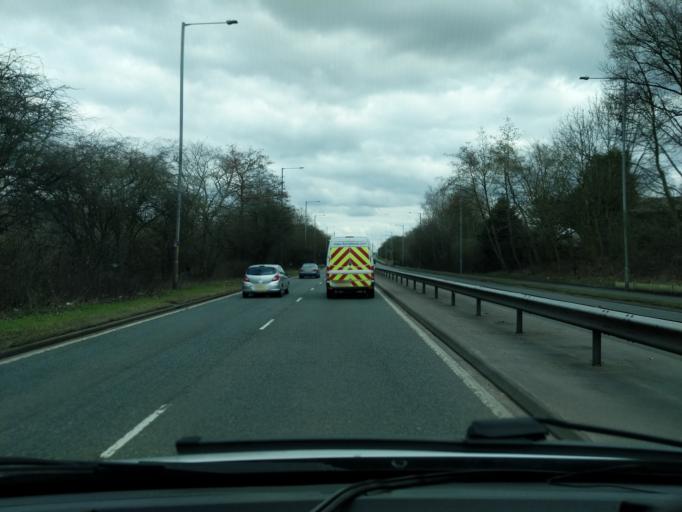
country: GB
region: England
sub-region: St. Helens
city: Billinge
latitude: 53.4729
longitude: -2.7129
